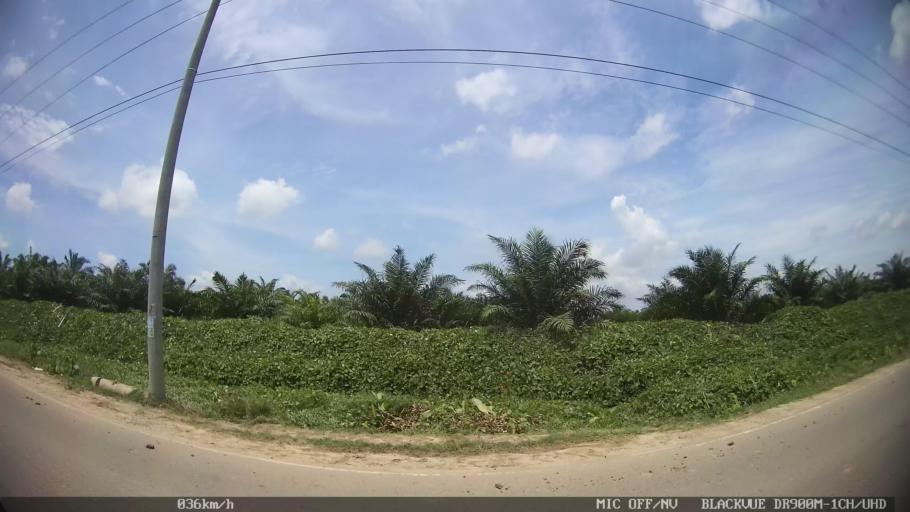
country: ID
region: North Sumatra
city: Perbaungan
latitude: 3.5256
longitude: 98.8888
